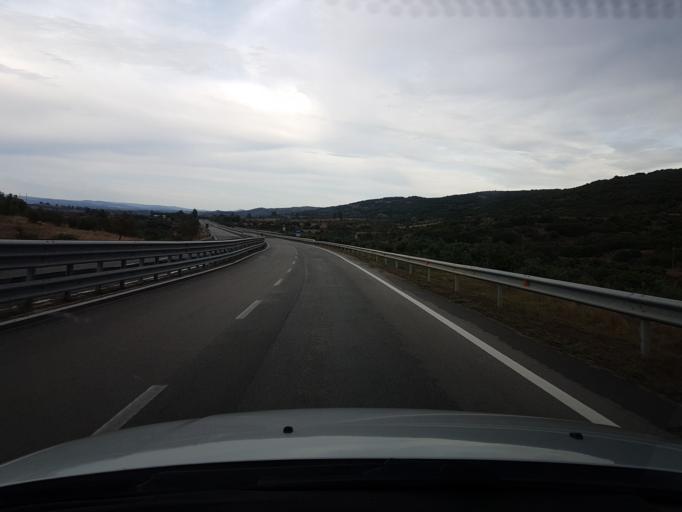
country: IT
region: Sardinia
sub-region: Provincia di Oristano
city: Sedilo
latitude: 40.1795
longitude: 8.9583
